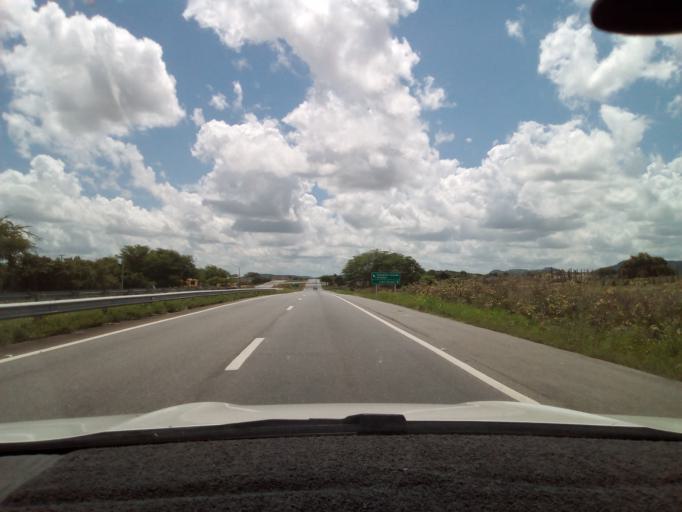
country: BR
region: Paraiba
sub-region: Mogeiro
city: Mogeiro
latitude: -7.2023
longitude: -35.4975
